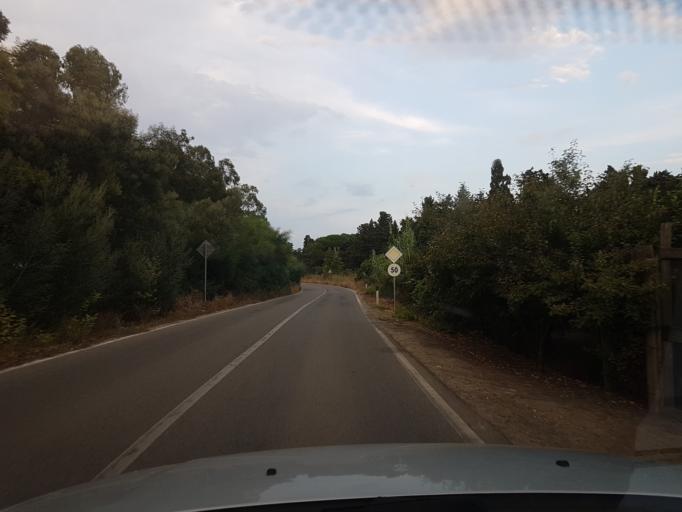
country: IT
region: Sardinia
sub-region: Provincia di Oristano
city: Solanas
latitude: 39.9312
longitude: 8.5559
